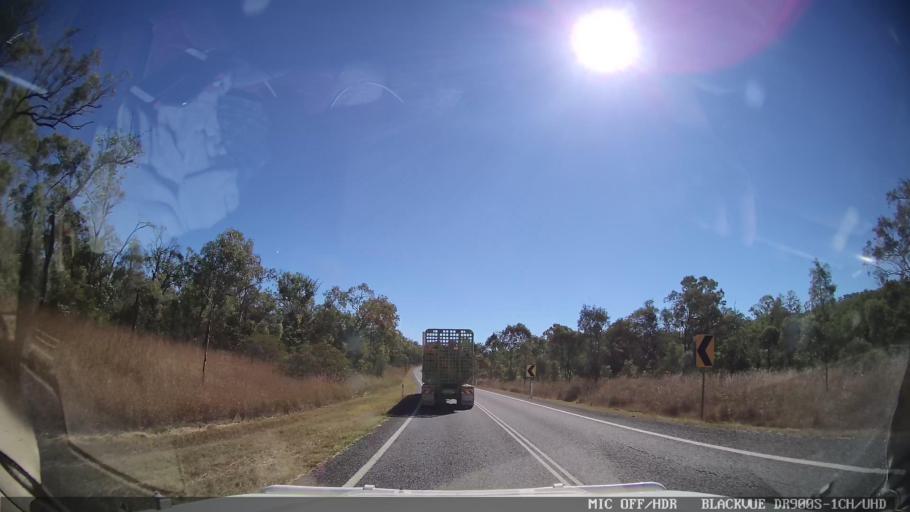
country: AU
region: Queensland
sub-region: Gladstone
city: Toolooa
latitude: -24.1504
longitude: 151.2093
